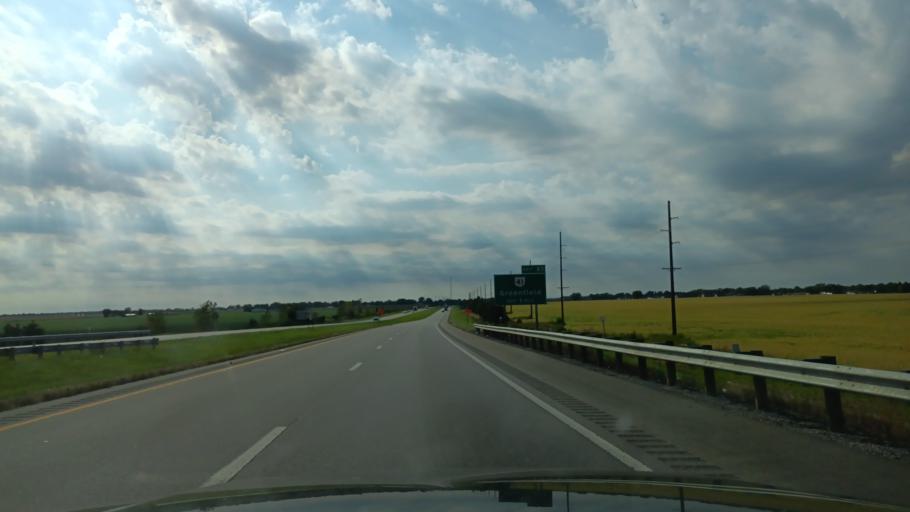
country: US
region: Ohio
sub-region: Fayette County
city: Washington Court House
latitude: 39.5128
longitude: -83.4187
